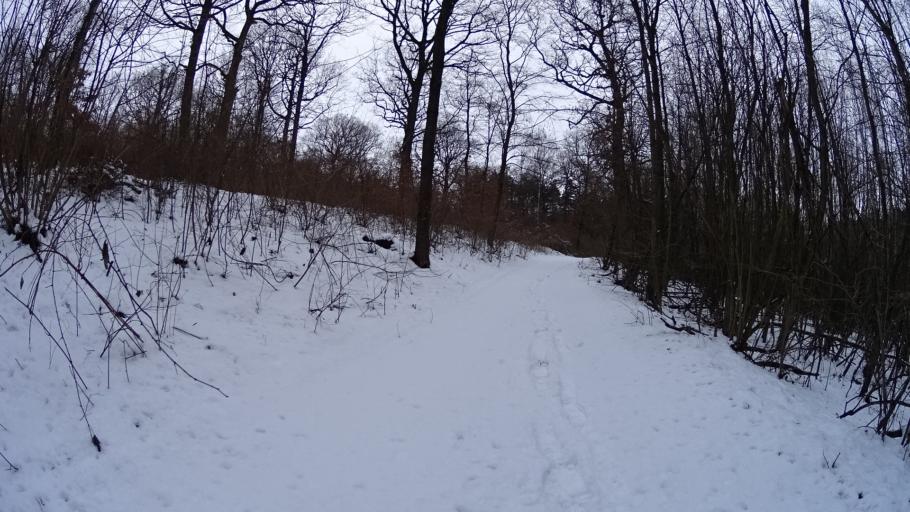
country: AT
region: Lower Austria
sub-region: Politischer Bezirk Korneuburg
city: Niederhollabrunn
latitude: 48.4206
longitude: 16.2901
